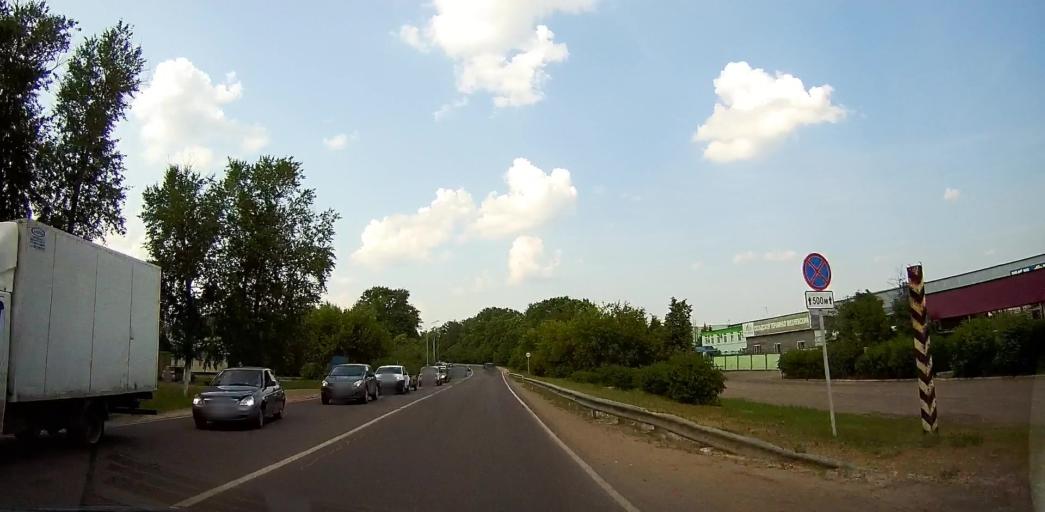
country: RU
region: Moskovskaya
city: Mikhnevo
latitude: 55.1389
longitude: 37.9498
